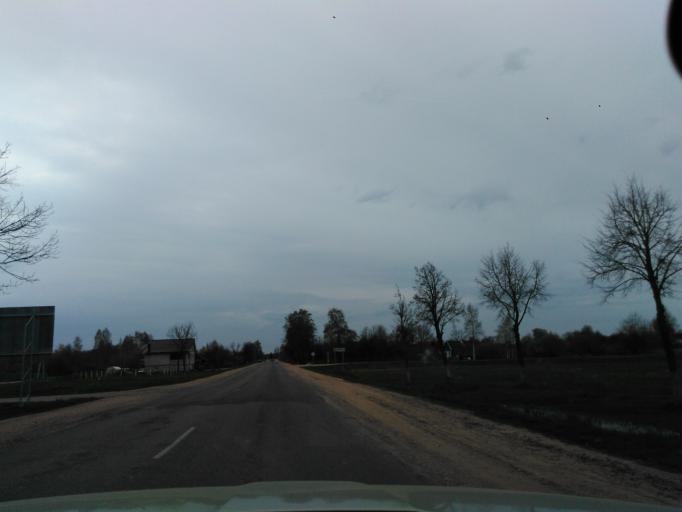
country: BY
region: Vitebsk
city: Chashniki
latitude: 54.8411
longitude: 29.1480
